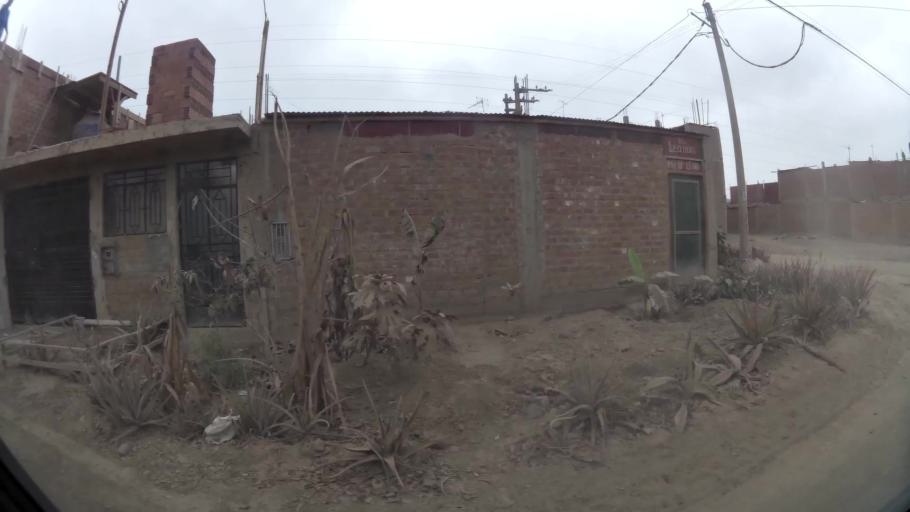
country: PE
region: Lima
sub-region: Lima
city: Independencia
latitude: -11.9556
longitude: -77.0974
